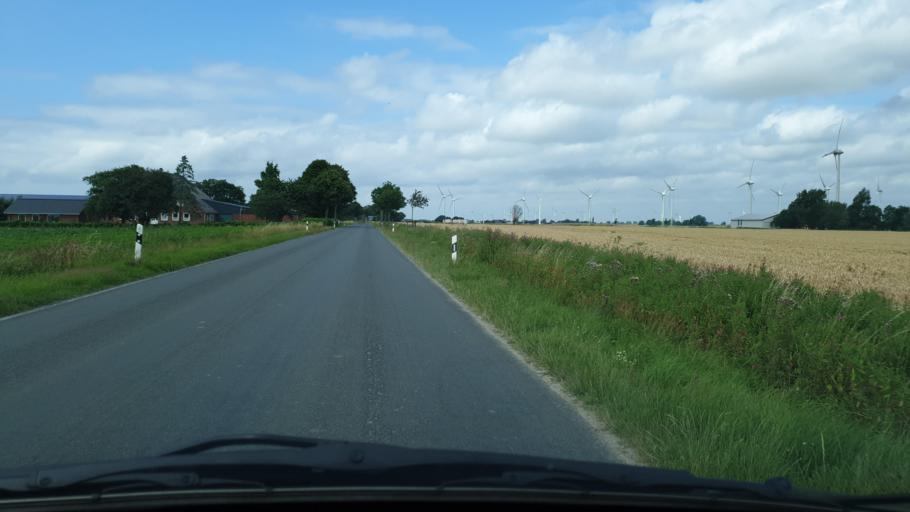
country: DE
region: Schleswig-Holstein
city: Kronprinzenkoog
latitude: 53.9659
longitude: 8.9291
